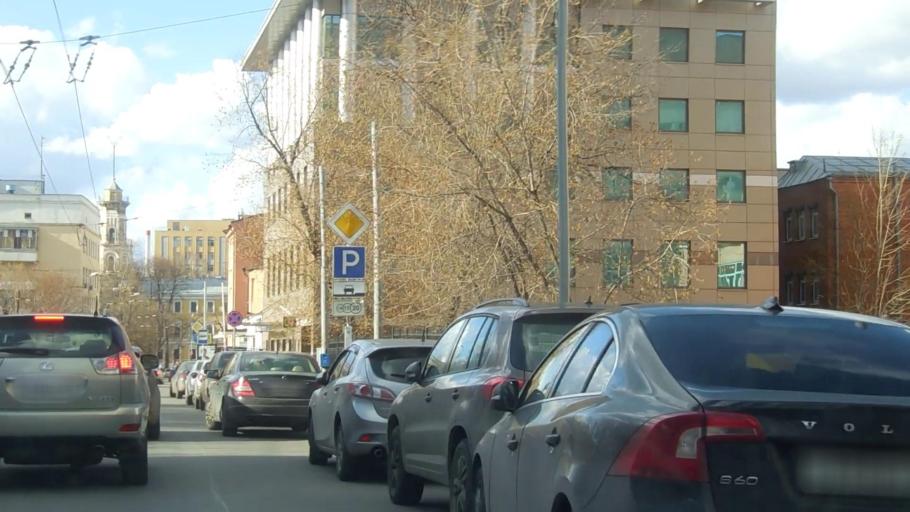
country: RU
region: Moscow
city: Mar'ina Roshcha
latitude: 55.7780
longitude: 37.6064
